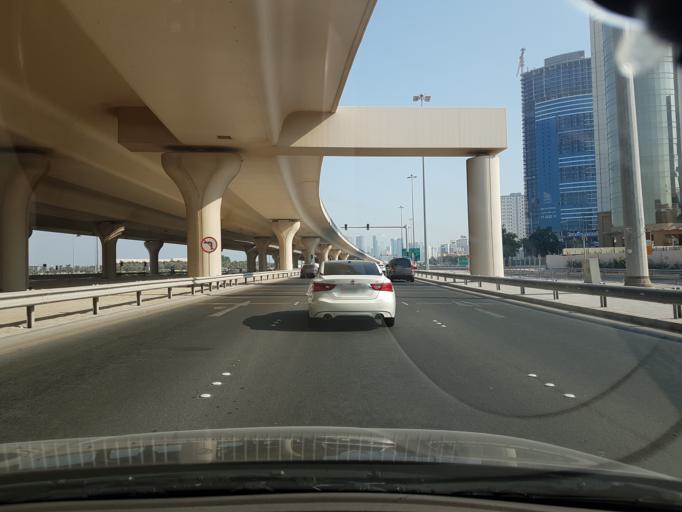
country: BH
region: Muharraq
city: Al Muharraq
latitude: 26.2443
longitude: 50.5919
